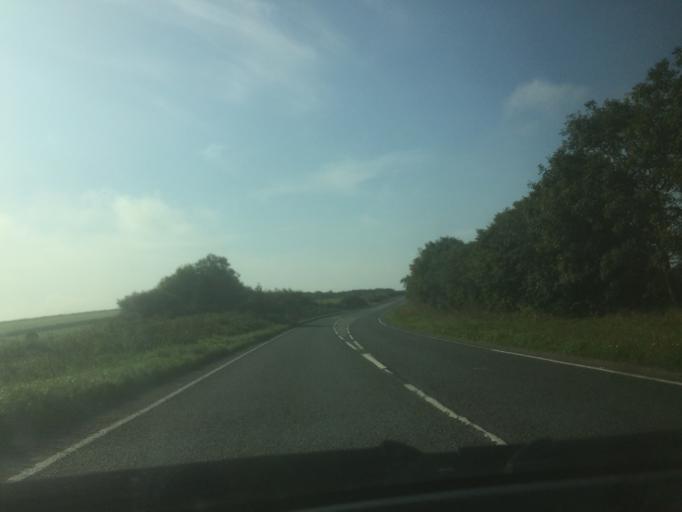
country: GB
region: England
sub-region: Cornwall
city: Callington
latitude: 50.4893
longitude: -4.2881
